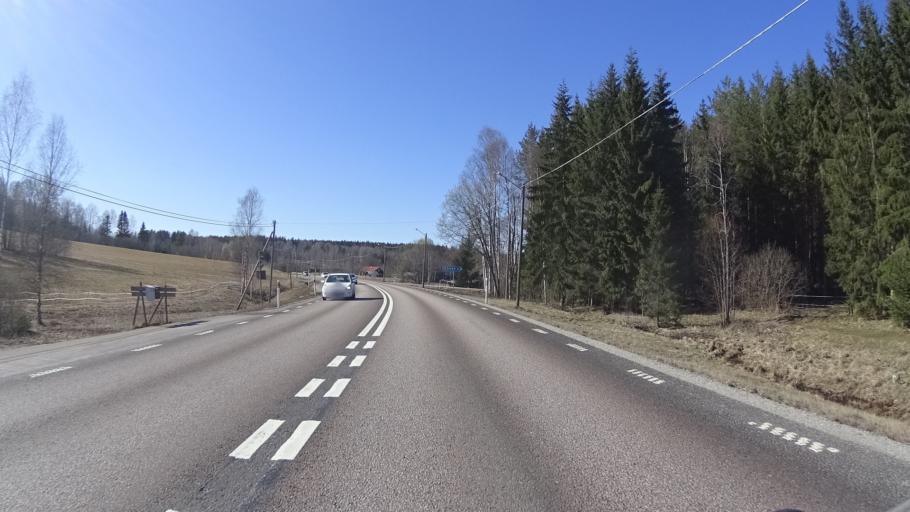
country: SE
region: Vaermland
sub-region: Sunne Kommun
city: Sunne
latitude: 59.6664
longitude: 12.9117
